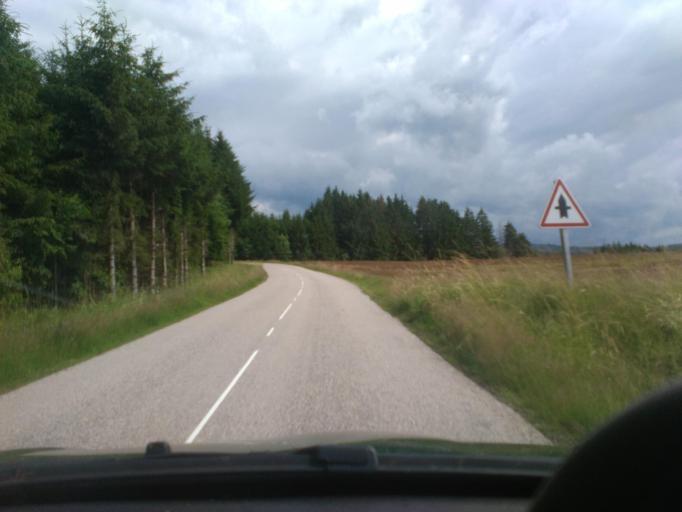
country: FR
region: Lorraine
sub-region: Departement des Vosges
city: Senones
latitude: 48.3972
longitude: 7.0294
